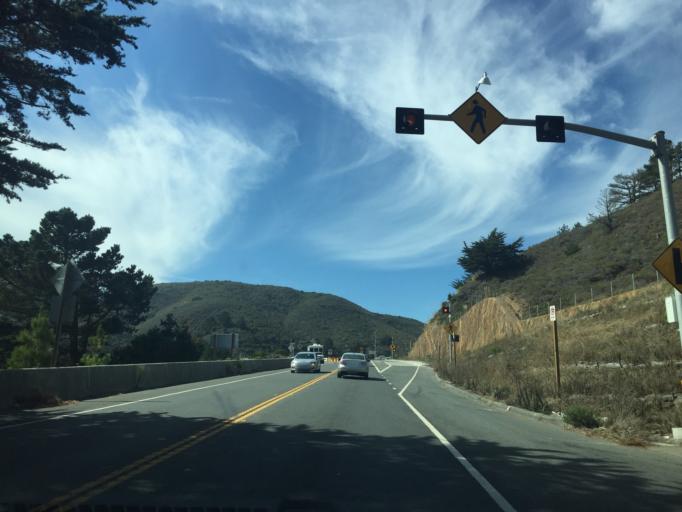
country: US
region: California
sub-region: San Mateo County
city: Pacifica
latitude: 37.5853
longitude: -122.5059
